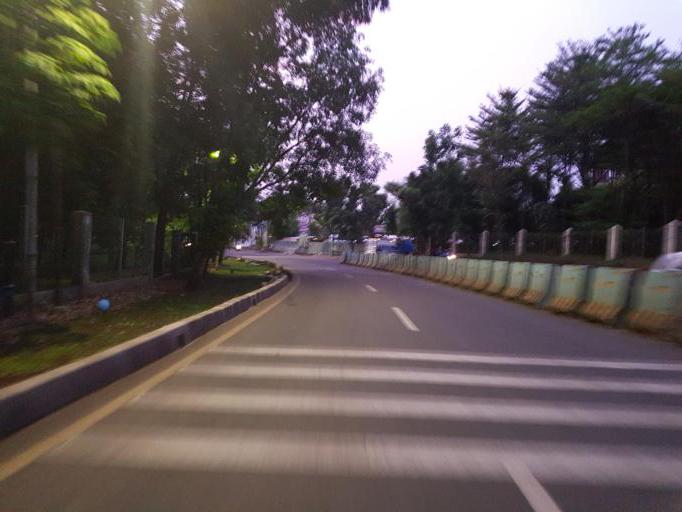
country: ID
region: West Java
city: Serpong
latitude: -6.3294
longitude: 106.6736
